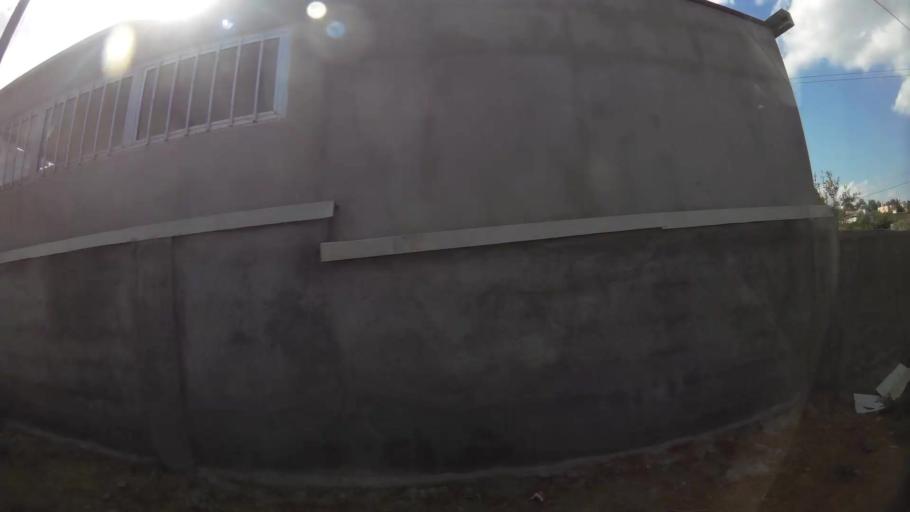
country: CY
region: Lefkosia
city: Nicosia
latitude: 35.2249
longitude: 33.3830
